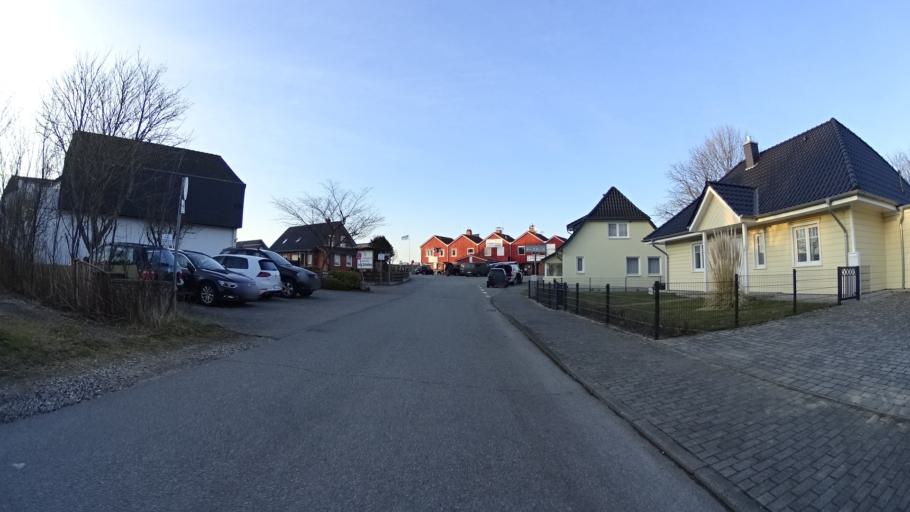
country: DE
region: Schleswig-Holstein
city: Stakendorf
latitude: 54.4104
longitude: 10.4206
